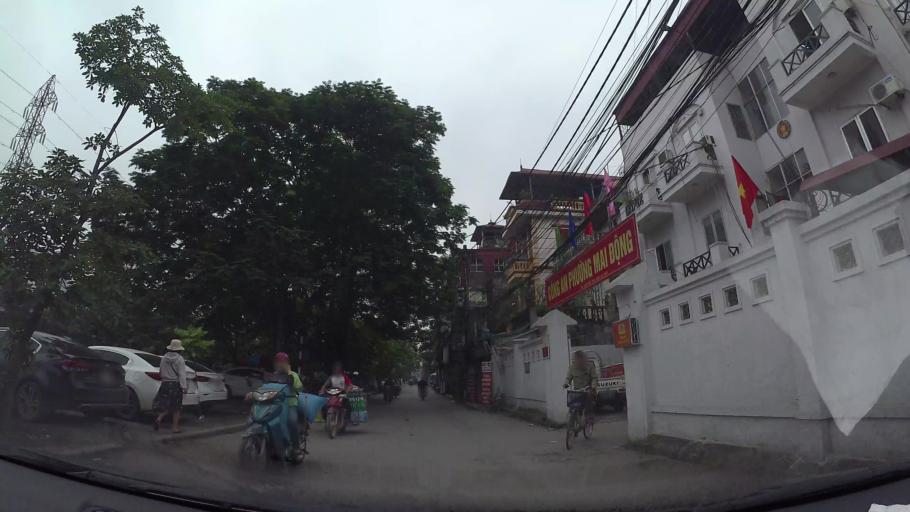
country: VN
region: Ha Noi
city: Hai BaTrung
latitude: 20.9910
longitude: 105.8626
